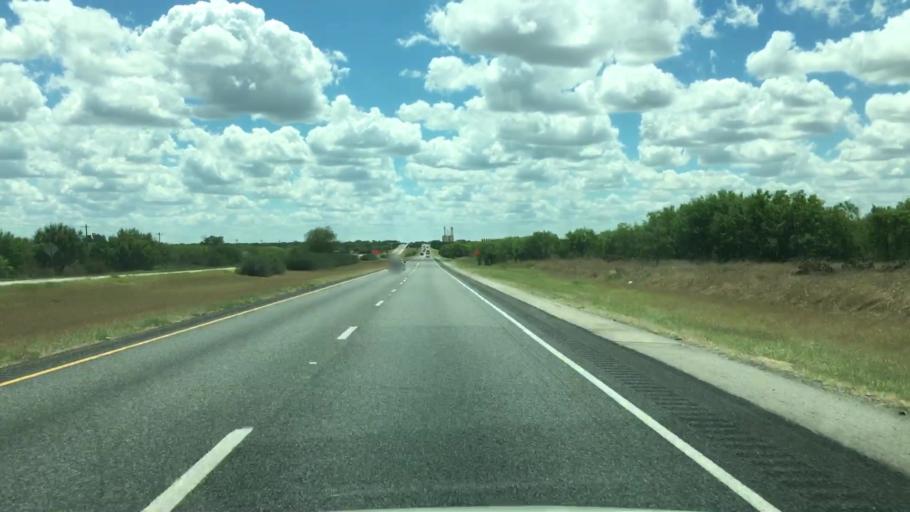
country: US
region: Texas
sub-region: Atascosa County
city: Pleasanton
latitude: 28.9738
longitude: -98.4349
